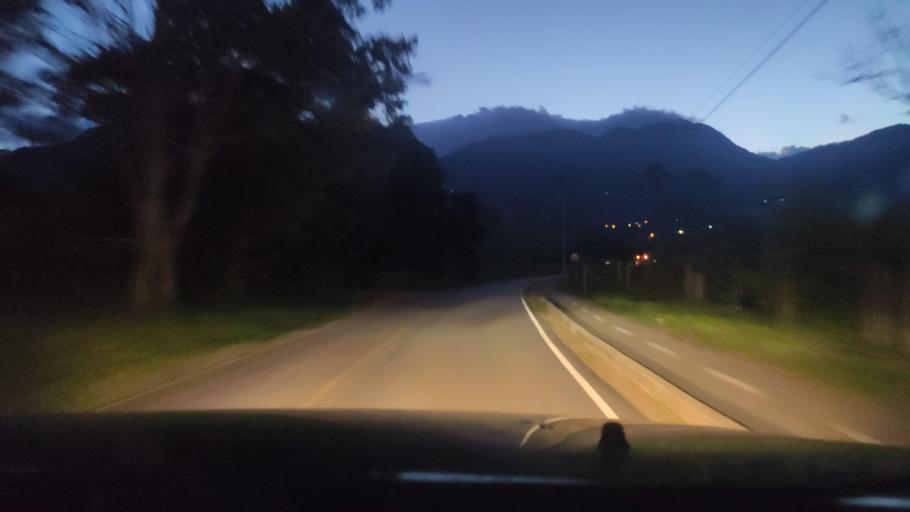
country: BR
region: Minas Gerais
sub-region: Paraisopolis
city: Paraisopolis
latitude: -22.7080
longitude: -45.7687
